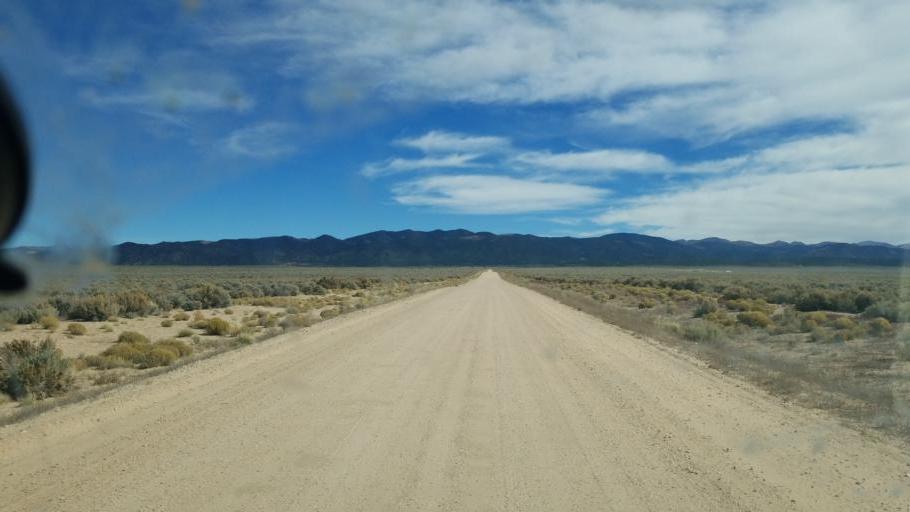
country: US
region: Colorado
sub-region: Costilla County
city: San Luis
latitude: 37.2869
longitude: -105.4449
